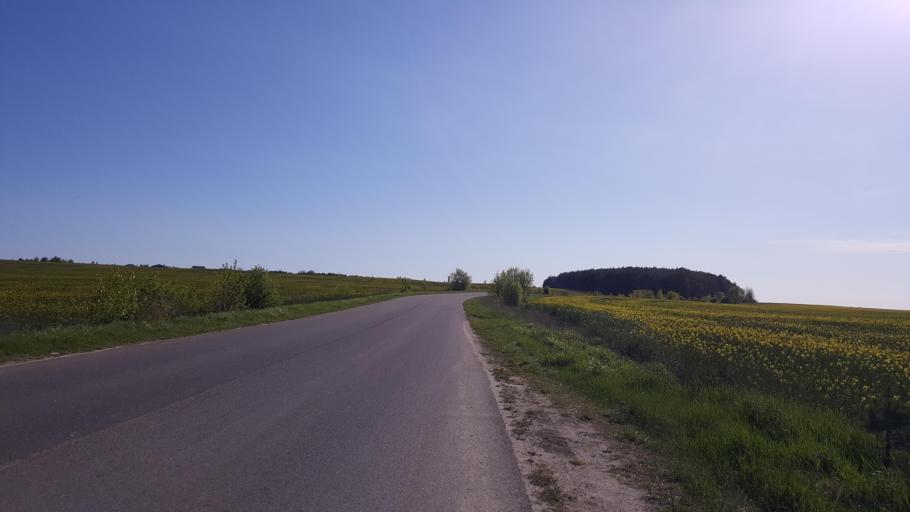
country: BY
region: Brest
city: Kamyanyets
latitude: 52.4114
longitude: 23.8536
